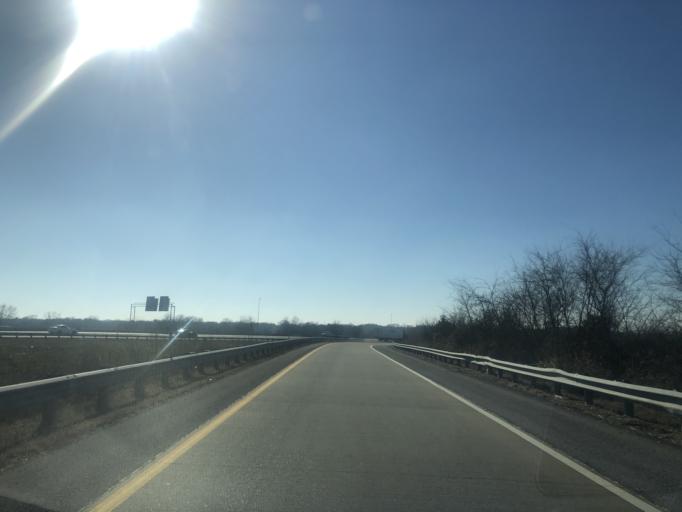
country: US
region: Tennessee
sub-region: Rutherford County
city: Murfreesboro
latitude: 35.9032
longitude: -86.4514
